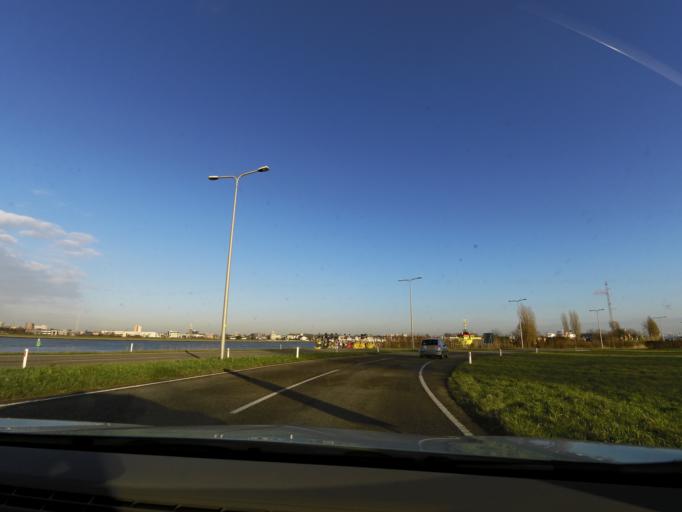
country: NL
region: South Holland
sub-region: Gemeente Maassluis
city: Maassluis
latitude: 51.9131
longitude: 4.2362
